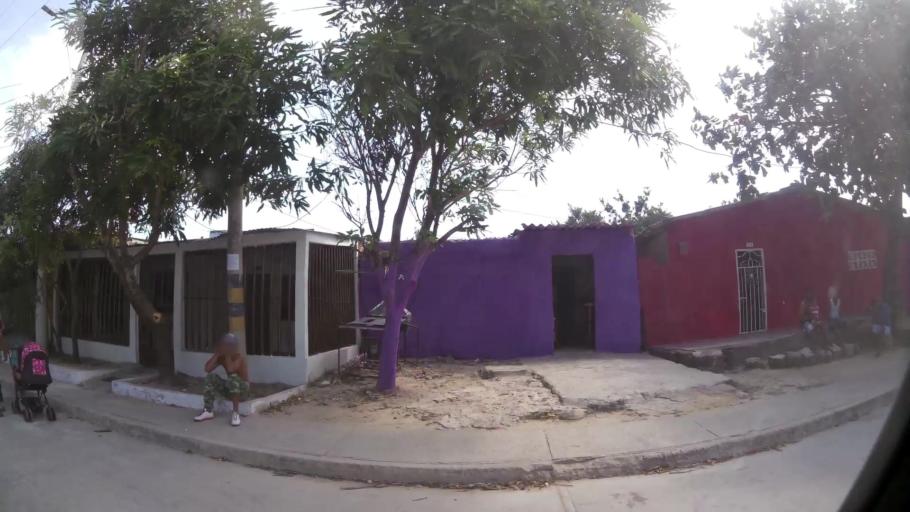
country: CO
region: Atlantico
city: Barranquilla
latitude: 10.9630
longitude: -74.8245
